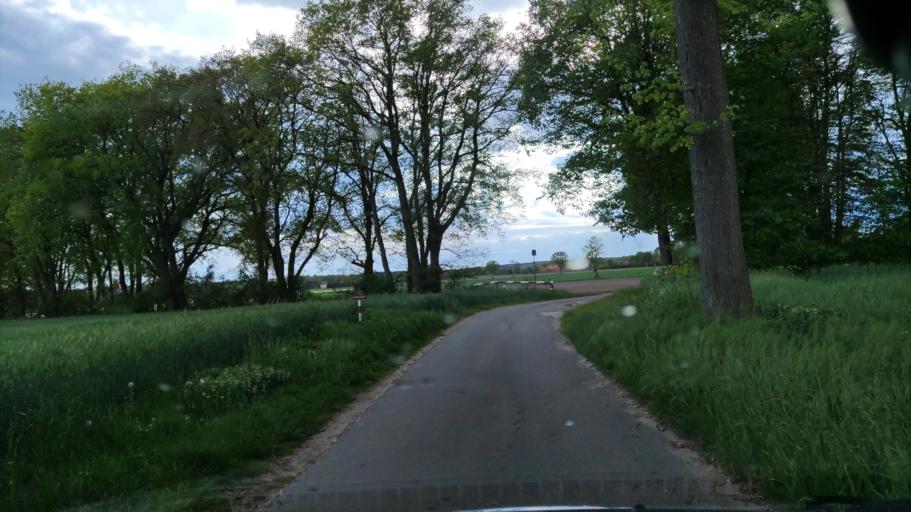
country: DE
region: Lower Saxony
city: Dahlenburg
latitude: 53.1751
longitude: 10.7229
